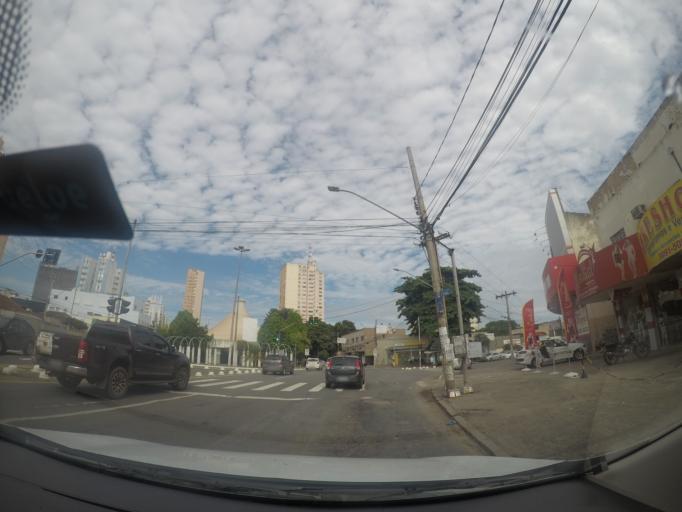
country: BR
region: Goias
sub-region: Goiania
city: Goiania
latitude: -16.6703
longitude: -49.2571
